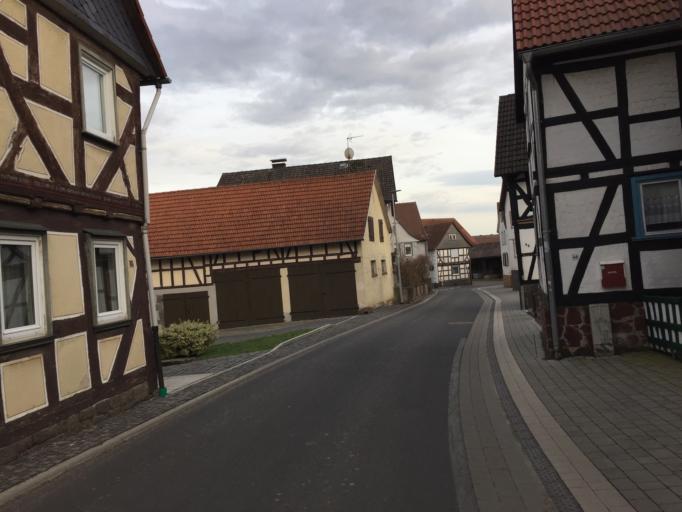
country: DE
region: Hesse
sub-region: Regierungsbezirk Giessen
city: Rabenau
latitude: 50.6912
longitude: 8.8427
